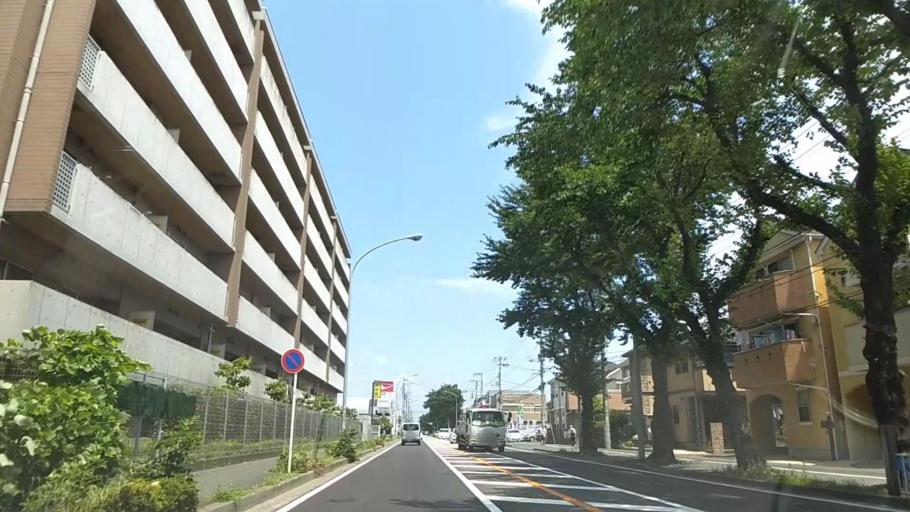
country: JP
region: Kanagawa
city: Minami-rinkan
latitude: 35.4755
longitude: 139.4806
